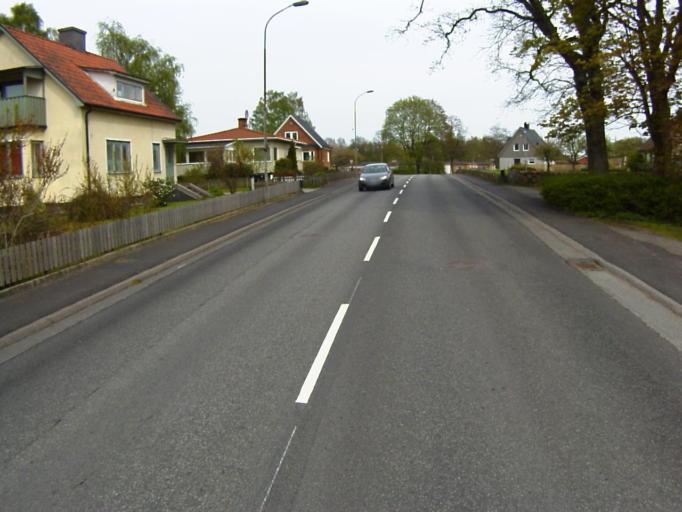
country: SE
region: Skane
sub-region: Kristianstads Kommun
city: Onnestad
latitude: 55.9325
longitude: 13.9854
